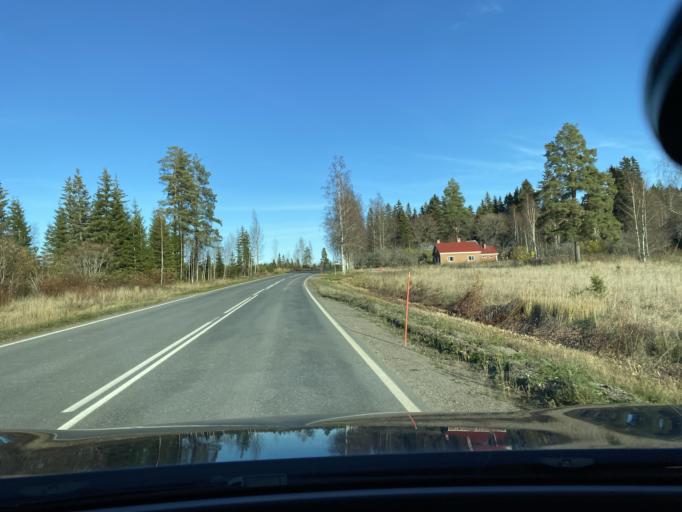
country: FI
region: Haeme
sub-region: Forssa
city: Tammela
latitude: 60.8494
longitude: 23.8407
